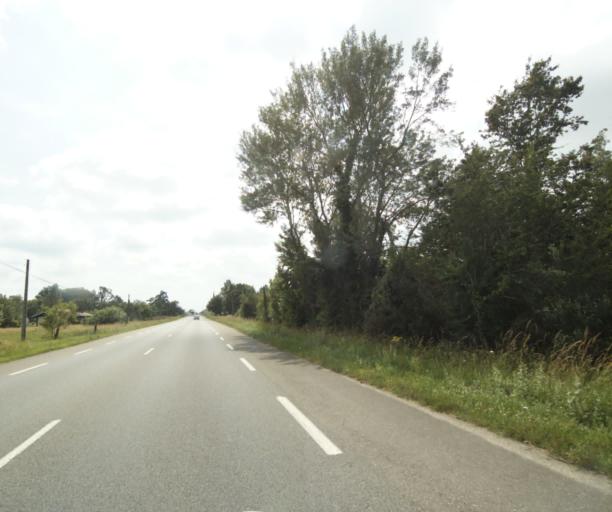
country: FR
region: Midi-Pyrenees
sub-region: Departement du Tarn-et-Garonne
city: Albias
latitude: 44.0636
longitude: 1.4133
